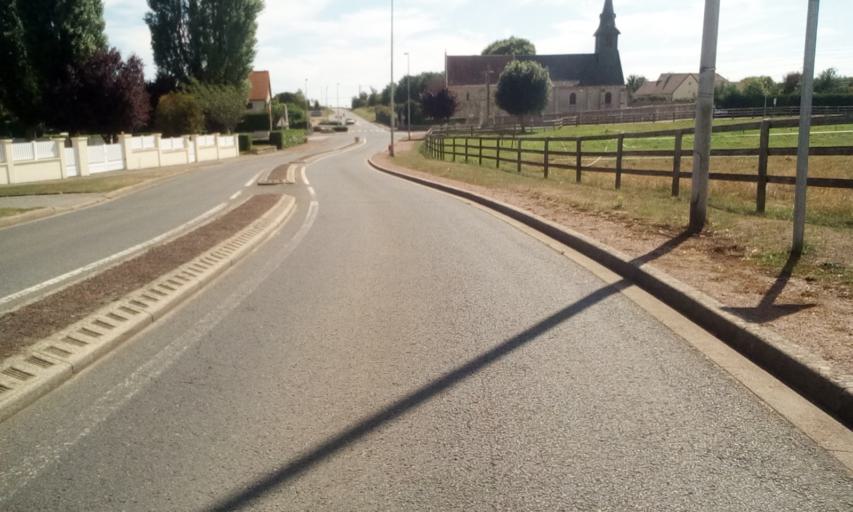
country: FR
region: Lower Normandy
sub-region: Departement du Calvados
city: Eterville
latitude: 49.1274
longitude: -0.4241
